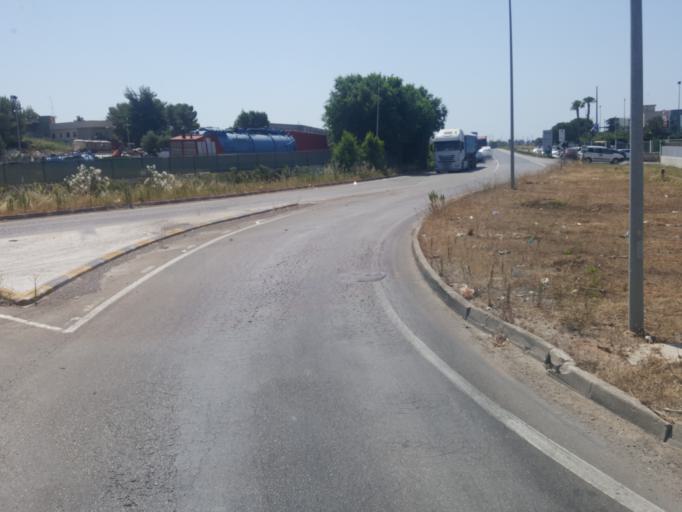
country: IT
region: Apulia
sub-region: Provincia di Taranto
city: Massafra
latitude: 40.5616
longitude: 17.1324
